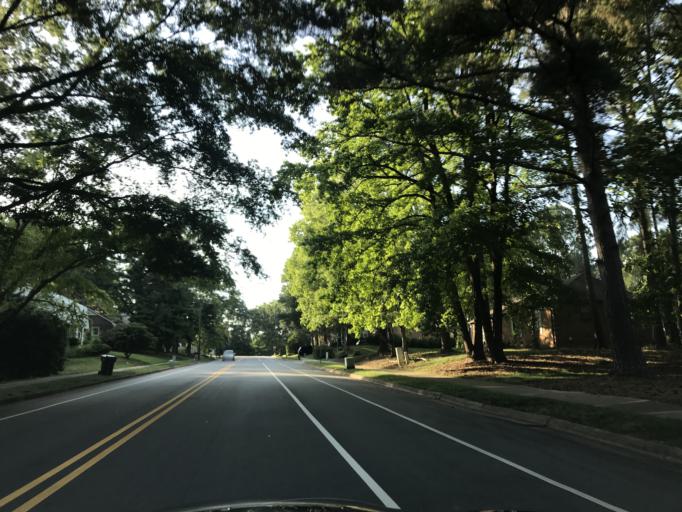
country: US
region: North Carolina
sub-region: Wake County
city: West Raleigh
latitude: 35.8259
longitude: -78.6907
